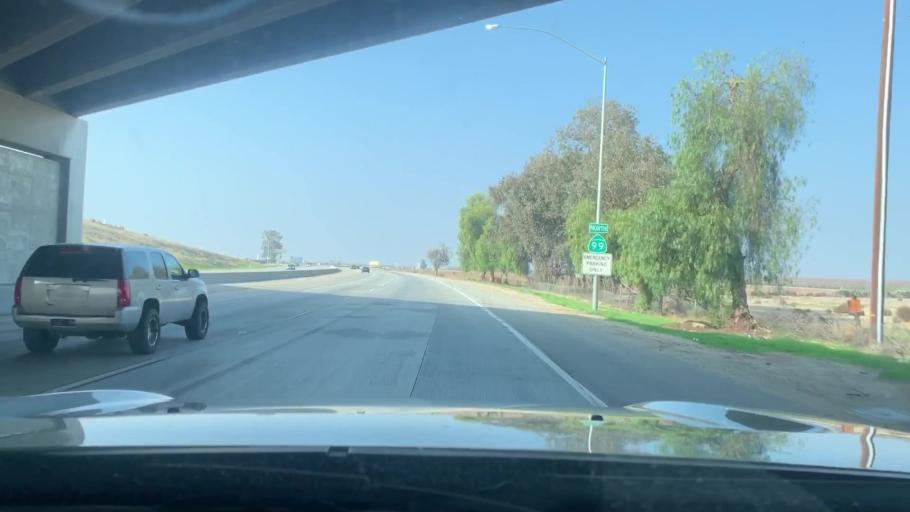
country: US
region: California
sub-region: Kern County
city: Shafter
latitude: 35.4998
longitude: -119.1633
